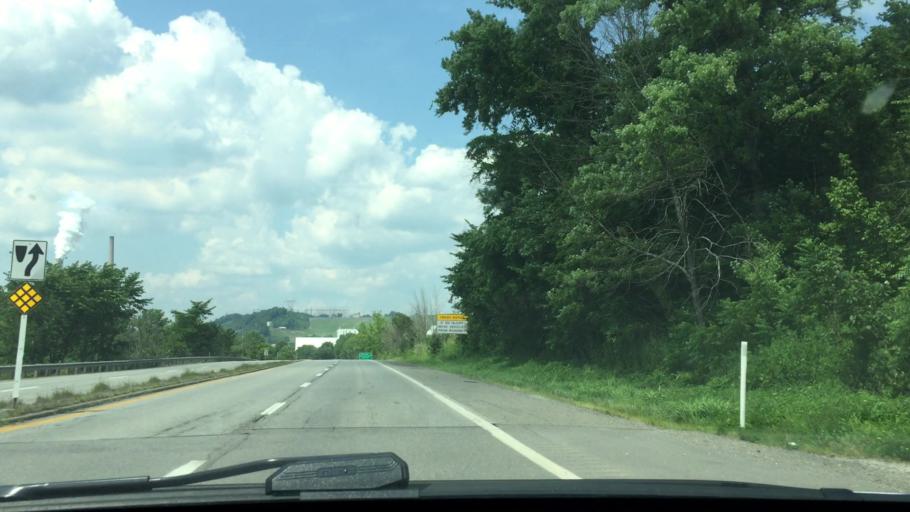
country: US
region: Ohio
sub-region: Belmont County
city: Powhatan Point
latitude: 39.8035
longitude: -80.8179
